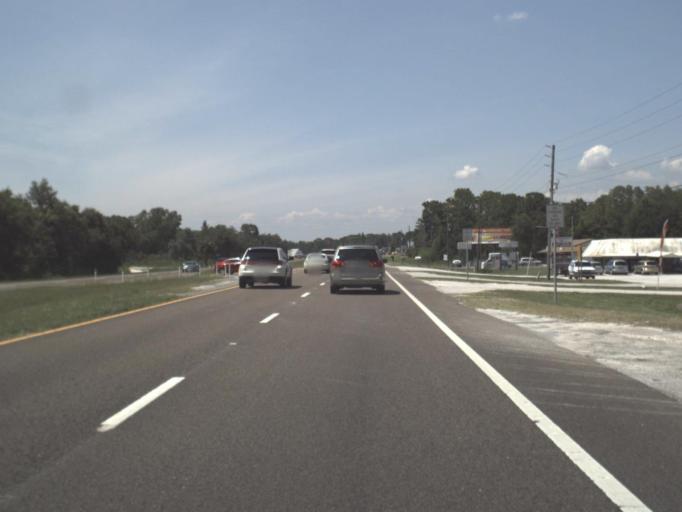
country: US
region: Florida
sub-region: Citrus County
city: Homosassa Springs
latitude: 28.7698
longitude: -82.5530
